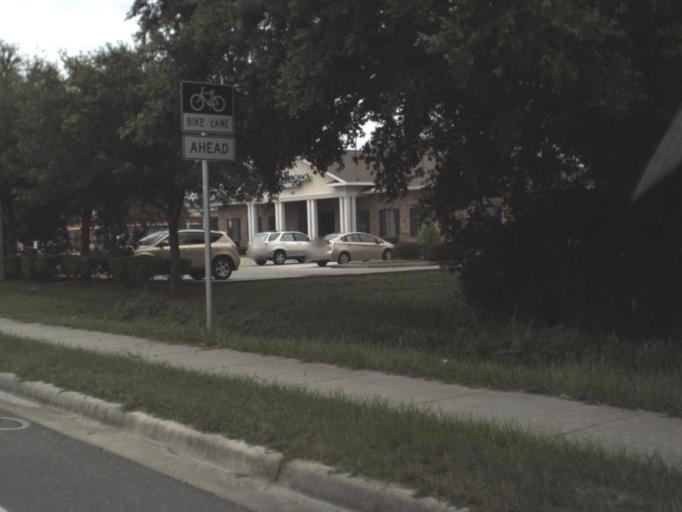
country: US
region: Florida
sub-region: Citrus County
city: Crystal River
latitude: 28.8986
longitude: -82.5748
